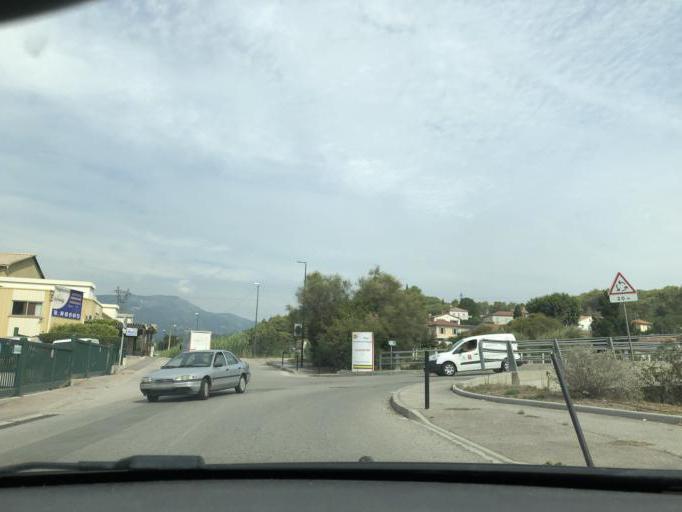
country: FR
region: Provence-Alpes-Cote d'Azur
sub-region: Departement des Alpes-Maritimes
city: Cantaron
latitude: 43.7811
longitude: 7.3369
